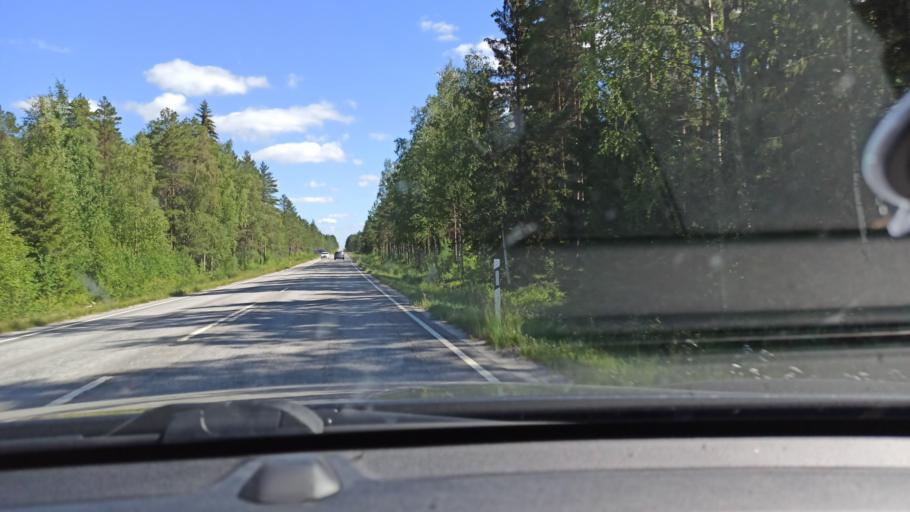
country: FI
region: Ostrobothnia
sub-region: Vaasa
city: Malax
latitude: 62.9754
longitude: 21.6044
